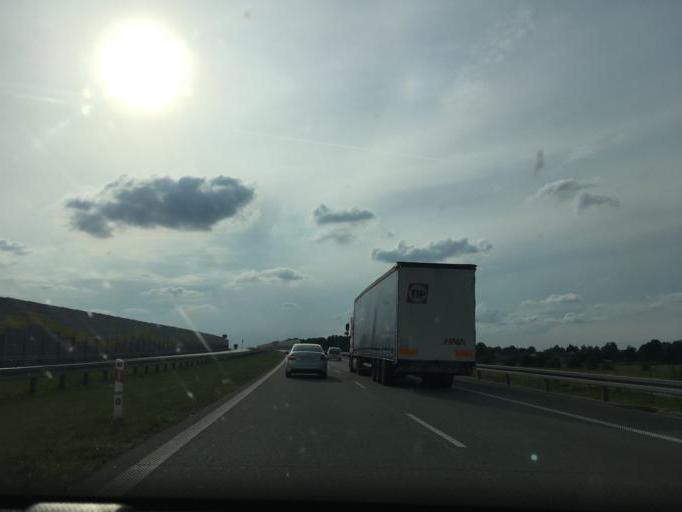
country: PL
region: Lodz Voivodeship
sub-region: Powiat pabianicki
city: Ksawerow
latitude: 51.6295
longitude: 19.4067
